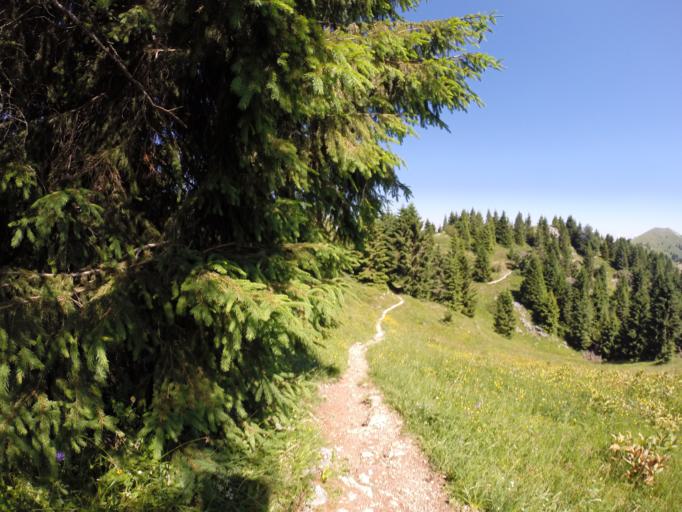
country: IT
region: Veneto
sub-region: Provincia di Treviso
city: Crespano del Grappa
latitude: 45.8901
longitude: 11.8119
